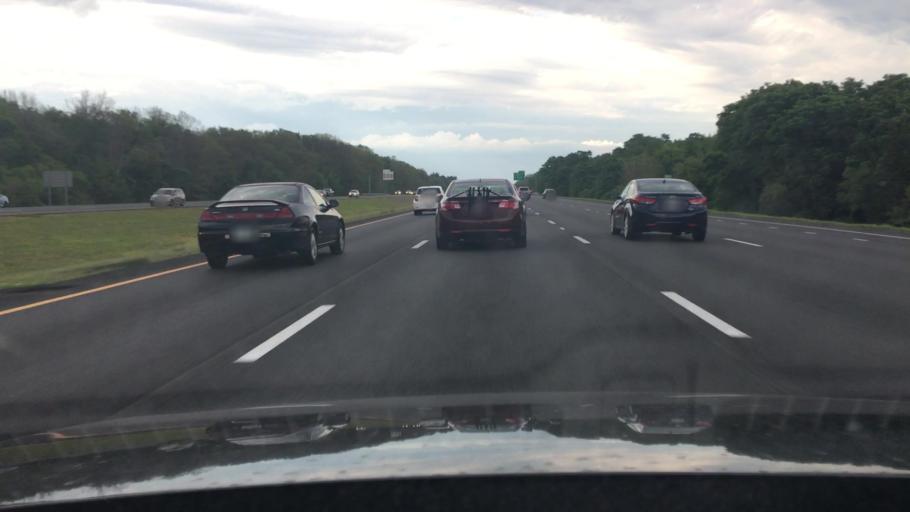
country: US
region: Massachusetts
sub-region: Essex County
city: West Newbury
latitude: 42.7617
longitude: -70.9382
